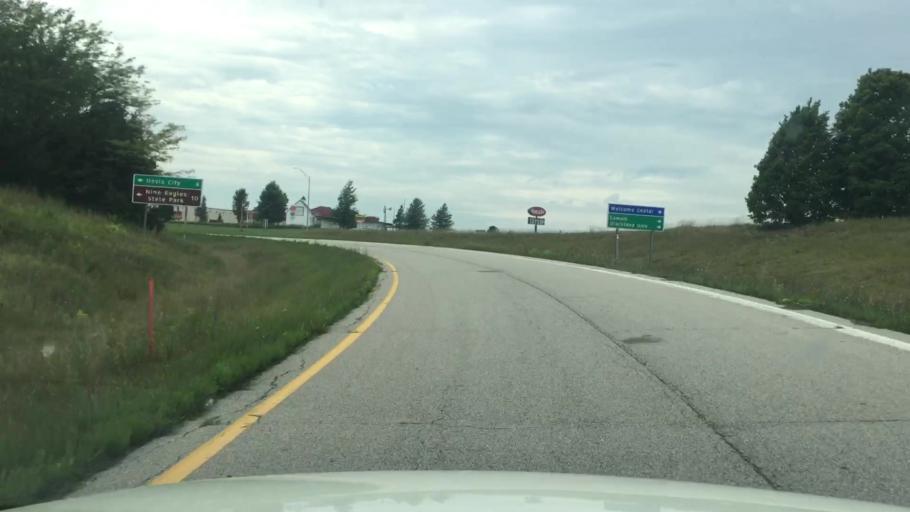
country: US
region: Iowa
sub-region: Decatur County
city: Lamoni
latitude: 40.6251
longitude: -93.8919
